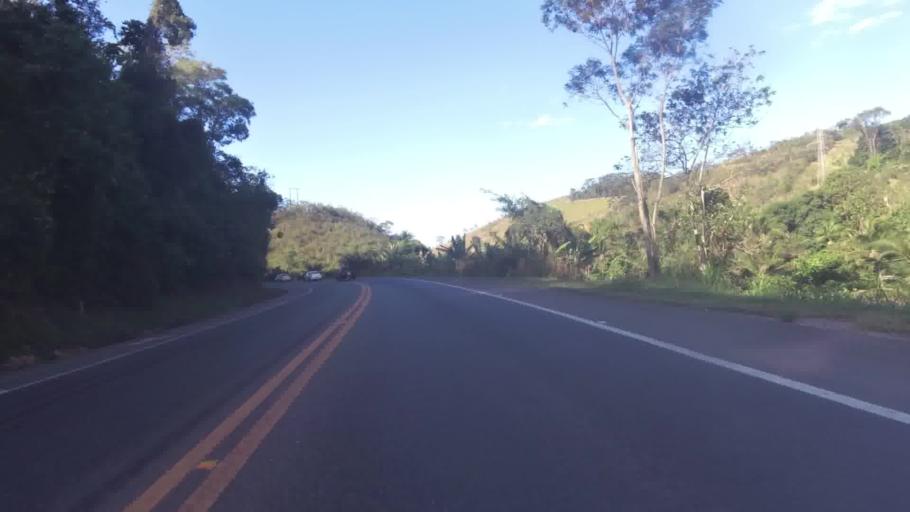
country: BR
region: Espirito Santo
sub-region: Iconha
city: Iconha
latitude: -20.8290
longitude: -40.8574
